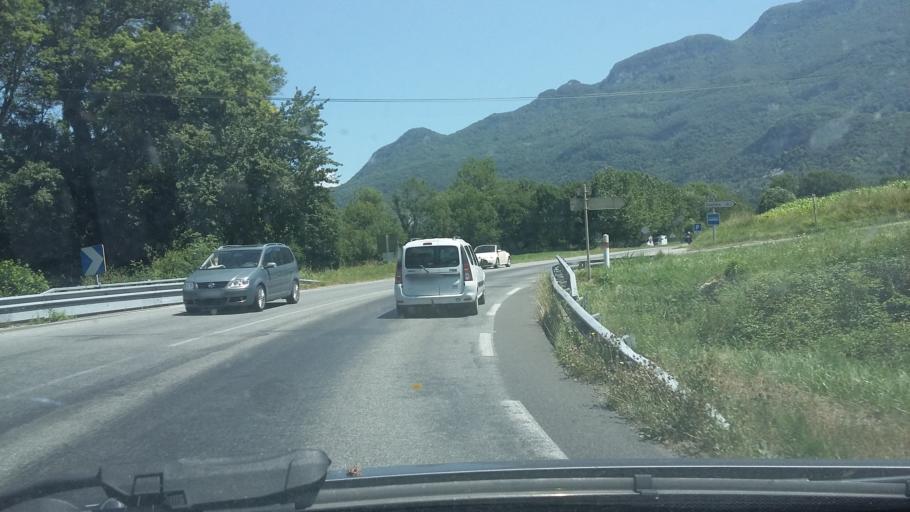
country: FR
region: Rhone-Alpes
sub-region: Departement de la Savoie
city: Yenne
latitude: 45.6972
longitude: 5.8016
